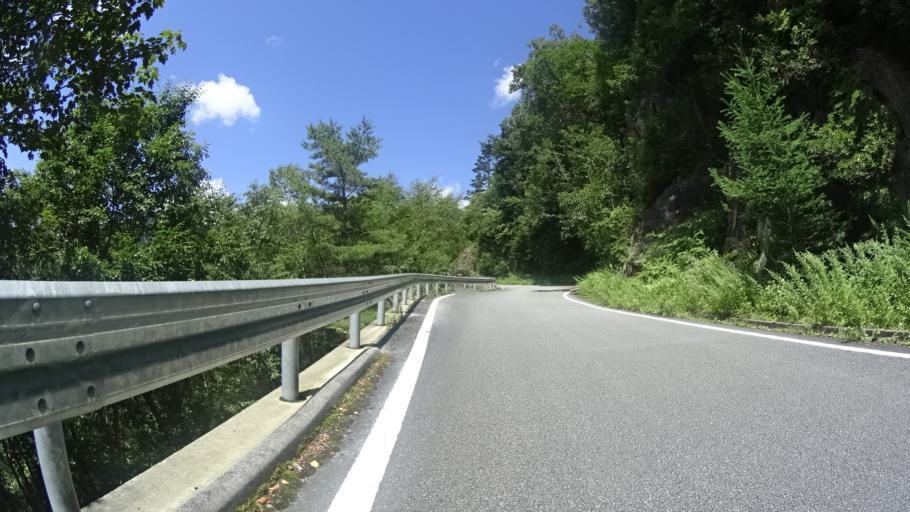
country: JP
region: Yamanashi
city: Enzan
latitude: 35.8480
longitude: 138.6427
